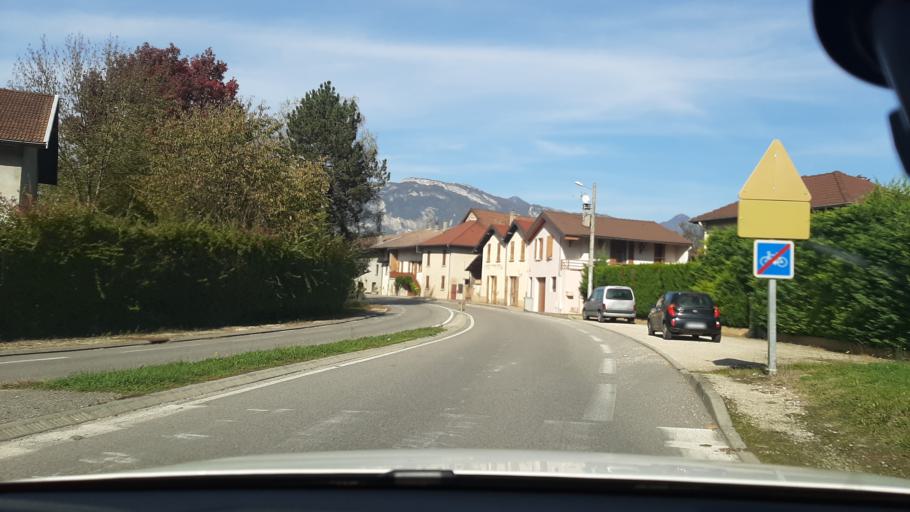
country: FR
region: Rhone-Alpes
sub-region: Departement de la Savoie
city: Montmelian
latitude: 45.4599
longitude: 6.0516
